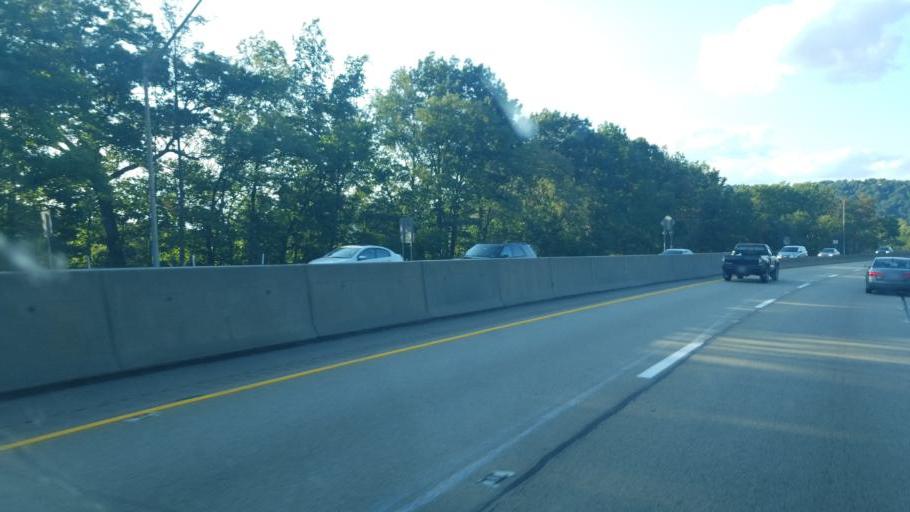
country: US
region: Pennsylvania
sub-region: Allegheny County
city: Coraopolis
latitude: 40.5050
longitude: -80.1377
